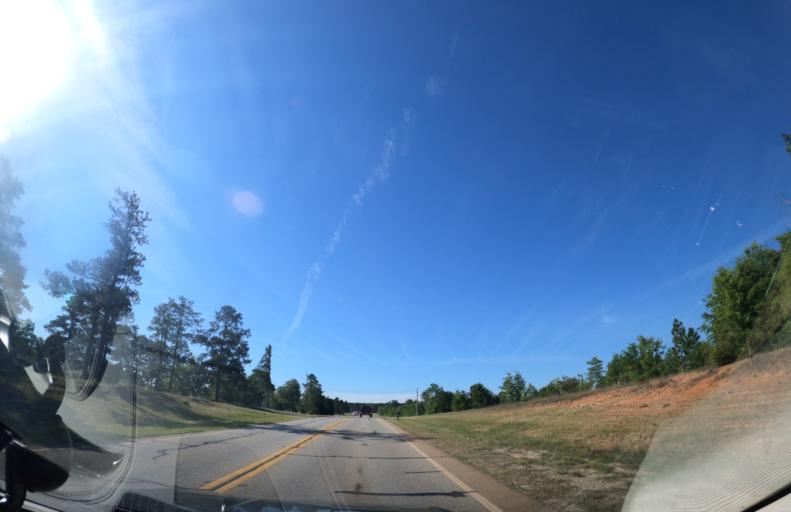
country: US
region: Georgia
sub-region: Jefferson County
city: Wrens
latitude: 33.2681
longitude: -82.3857
